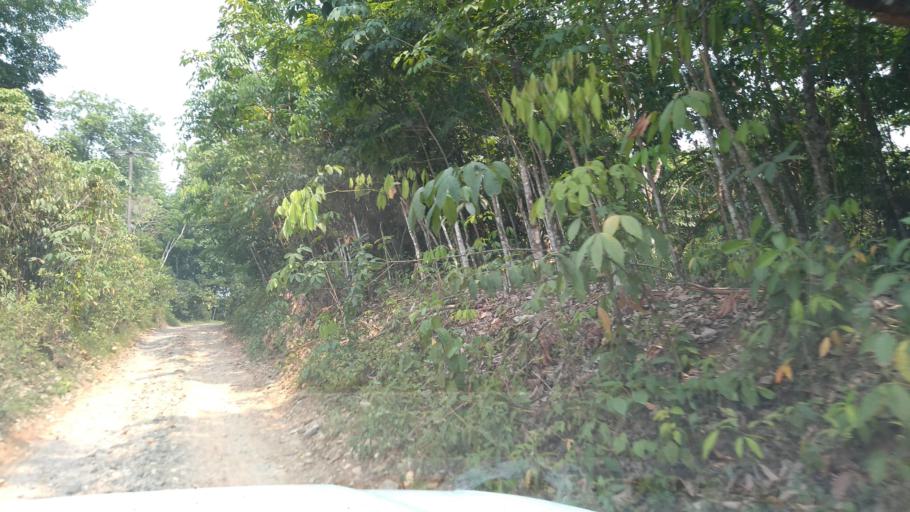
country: MX
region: Veracruz
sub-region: Tezonapa
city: Laguna Chica (Pueblo Nuevo)
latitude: 18.5507
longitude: -96.7832
